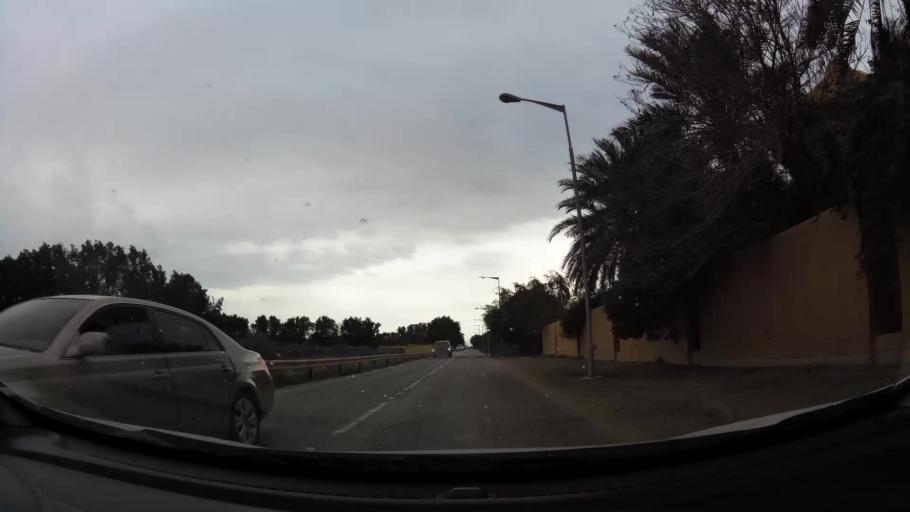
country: BH
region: Central Governorate
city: Madinat Hamad
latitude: 26.1554
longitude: 50.4623
